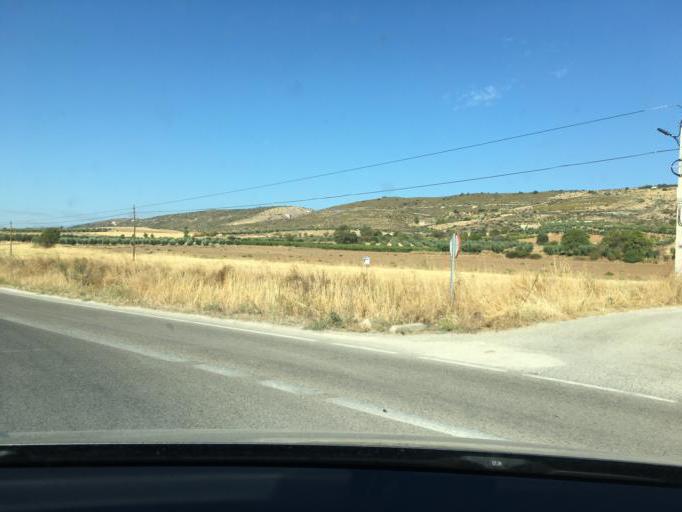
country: ES
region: Madrid
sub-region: Provincia de Madrid
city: Torremocha de Jarama
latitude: 40.8420
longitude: -3.5042
